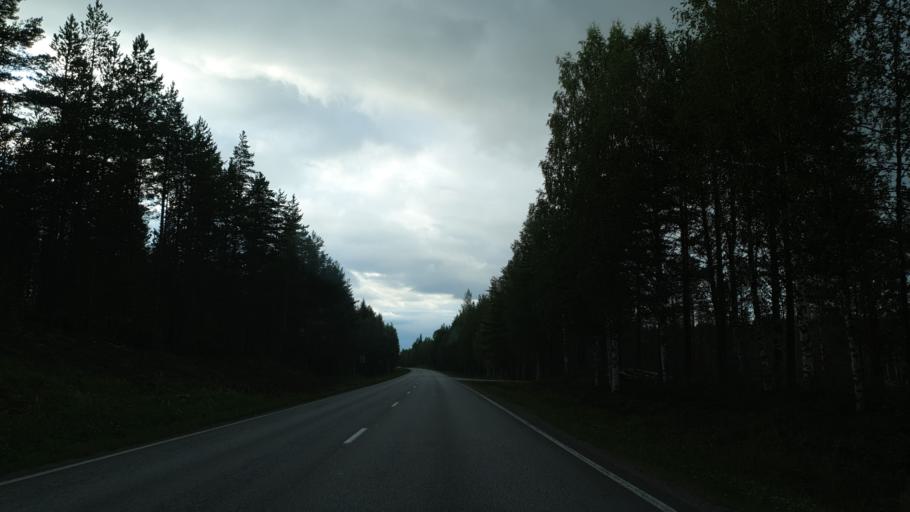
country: FI
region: North Karelia
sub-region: Pielisen Karjala
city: Lieksa
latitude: 63.0941
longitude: 30.1273
